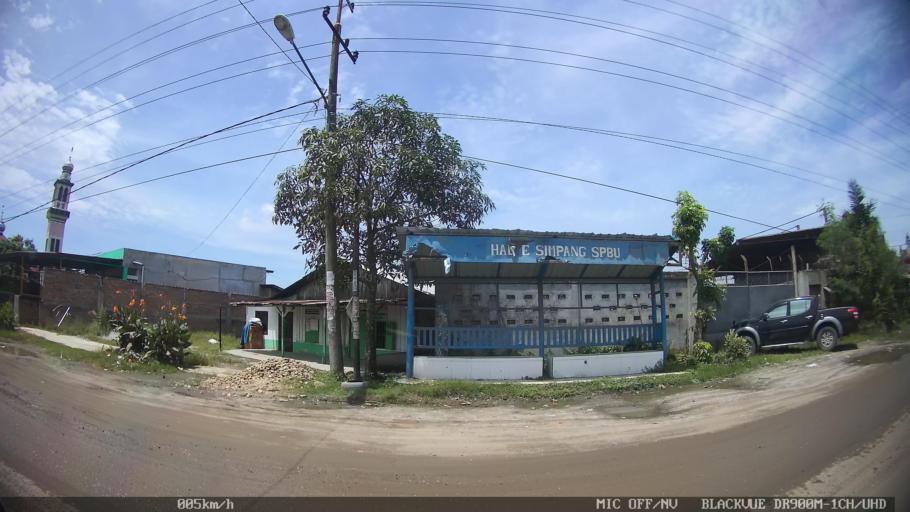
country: ID
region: North Sumatra
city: Perbaungan
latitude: 3.5450
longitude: 98.8807
